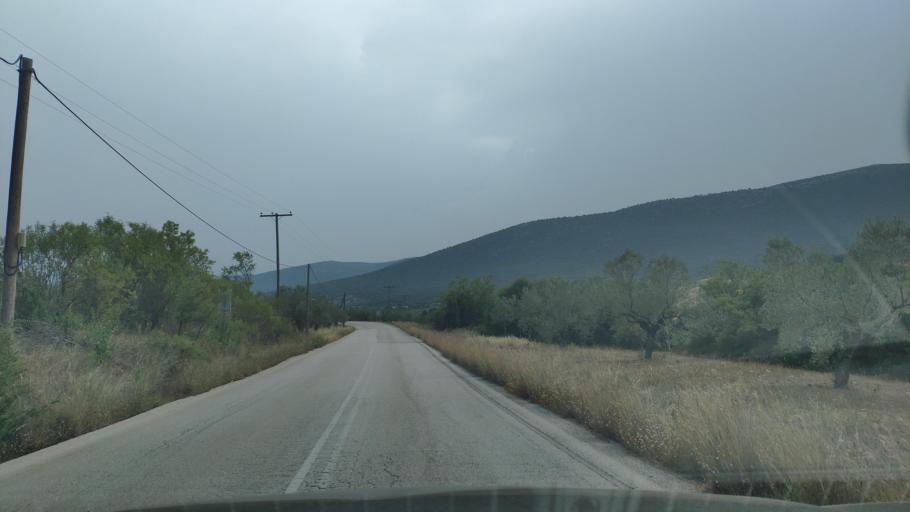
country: GR
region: Peloponnese
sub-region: Nomos Argolidos
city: Palaia Epidavros
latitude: 37.5775
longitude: 23.1514
